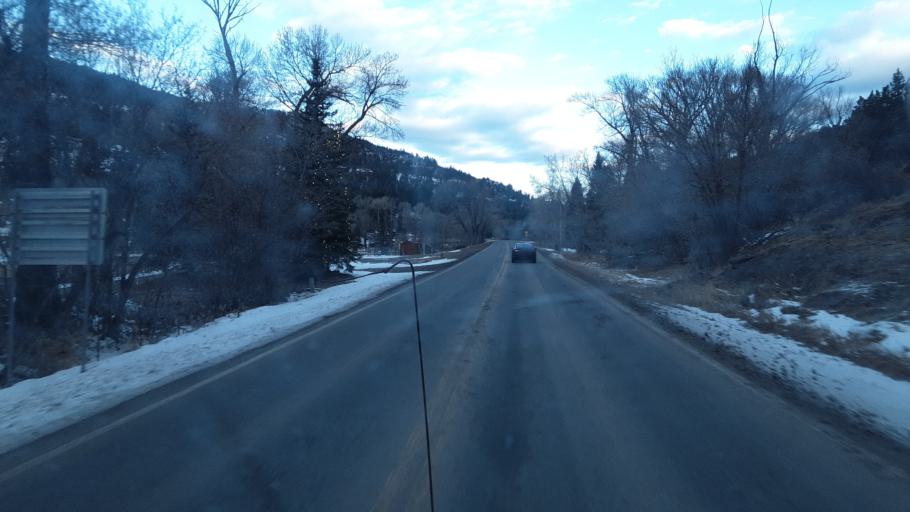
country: US
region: Colorado
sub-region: Ouray County
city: Ouray
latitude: 38.0506
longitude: -107.6845
